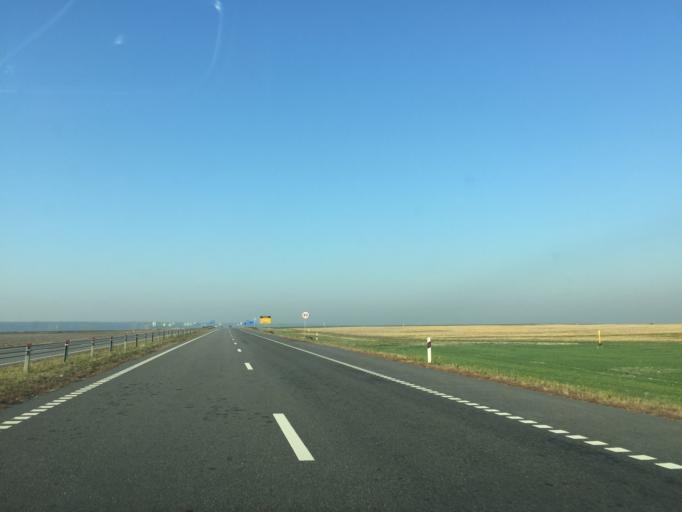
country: BY
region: Gomel
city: Kastsyukowka
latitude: 52.4868
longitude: 30.7875
